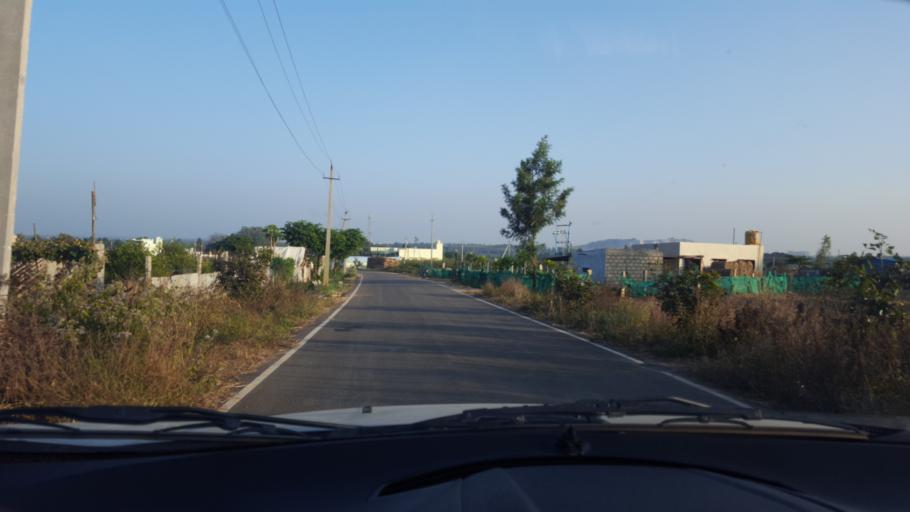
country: IN
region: Karnataka
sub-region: Bangalore Urban
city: Yelahanka
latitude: 13.1886
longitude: 77.6051
